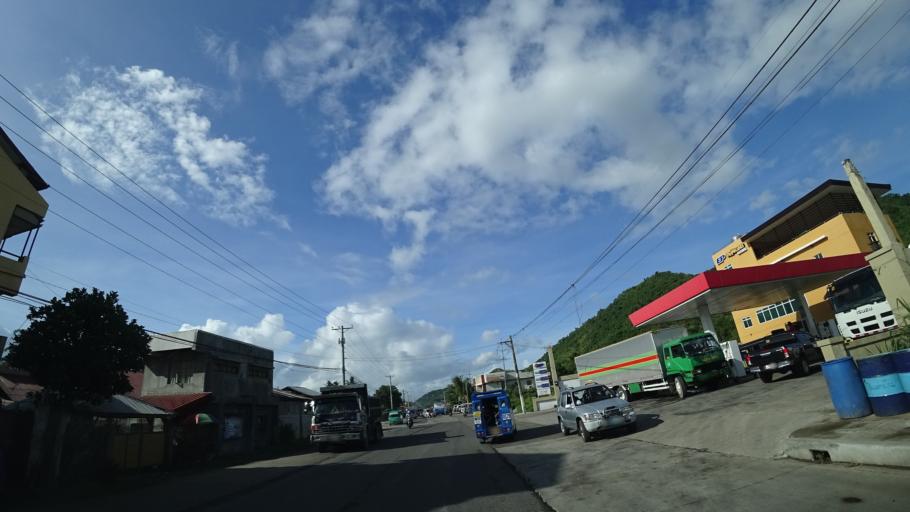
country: PH
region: Eastern Visayas
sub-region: Province of Leyte
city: Pawing
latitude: 11.2066
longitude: 124.9914
